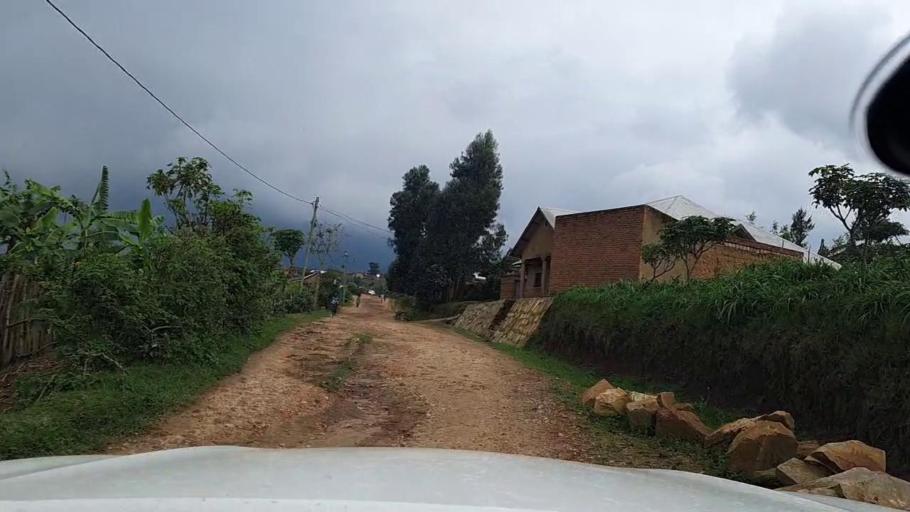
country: RW
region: Western Province
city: Kibuye
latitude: -2.1025
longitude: 29.4852
